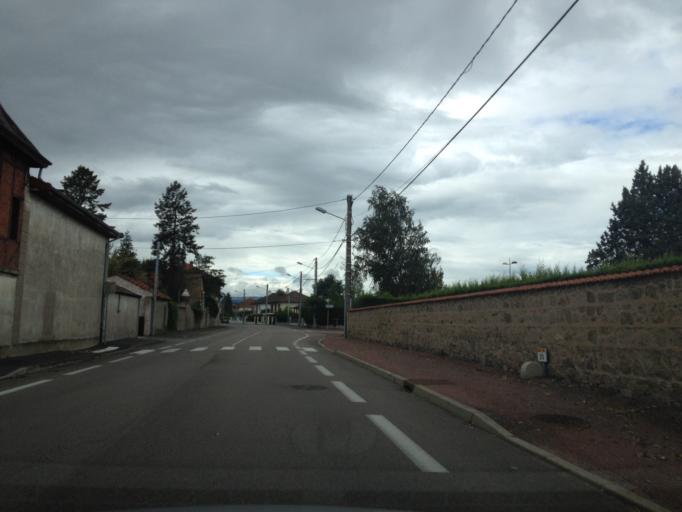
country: FR
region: Rhone-Alpes
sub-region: Departement de la Loire
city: Riorges
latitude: 46.0400
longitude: 4.0328
